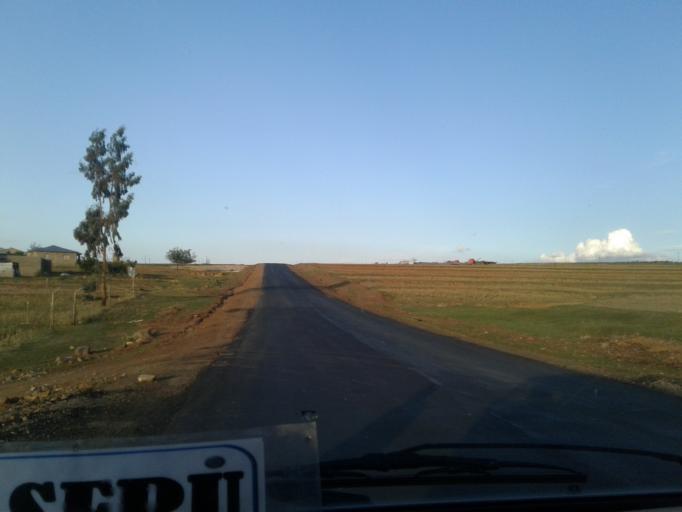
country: LS
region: Maseru
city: Maseru
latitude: -29.3121
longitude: 27.5966
